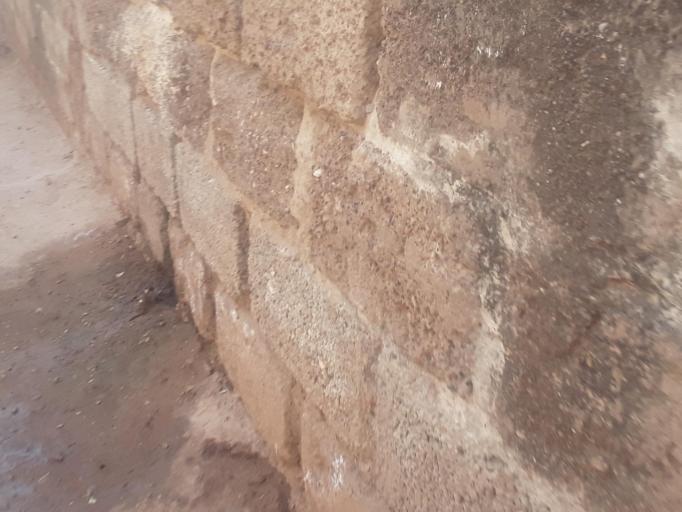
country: ZM
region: Lusaka
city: Lusaka
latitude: -15.3584
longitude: 28.2897
